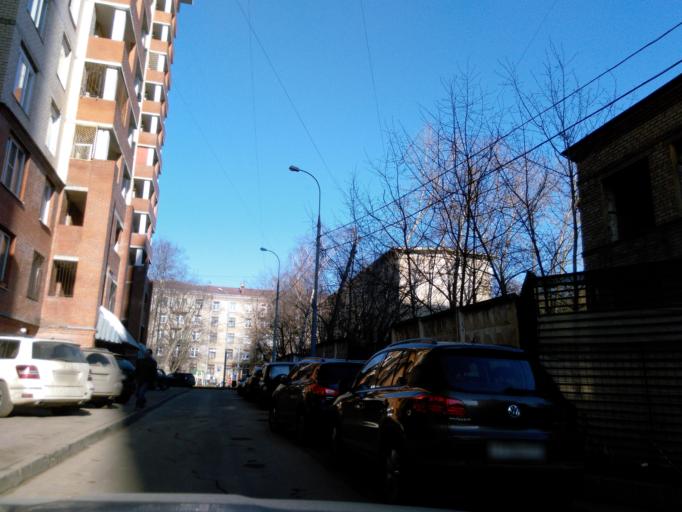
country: RU
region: Moskovskaya
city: Koptevo
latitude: 55.8179
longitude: 37.5256
